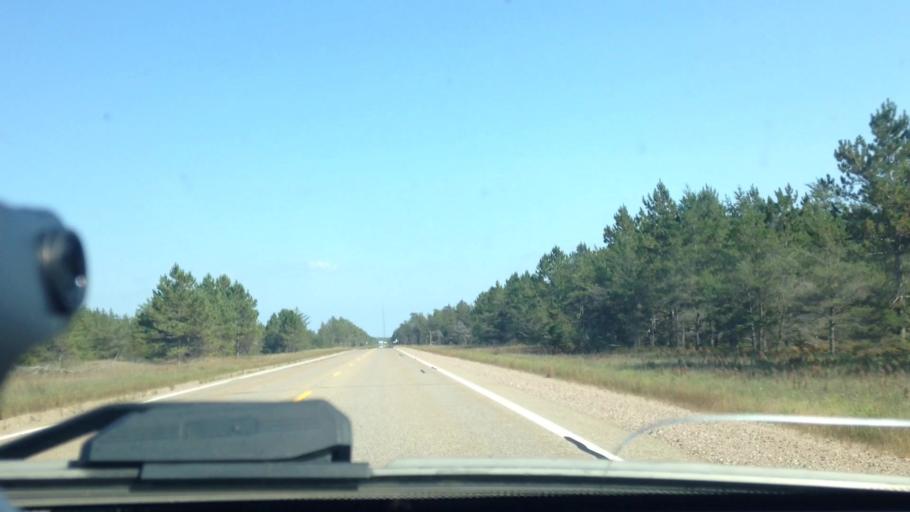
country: US
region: Michigan
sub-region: Chippewa County
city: Sault Ste. Marie
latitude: 46.3587
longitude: -84.8287
